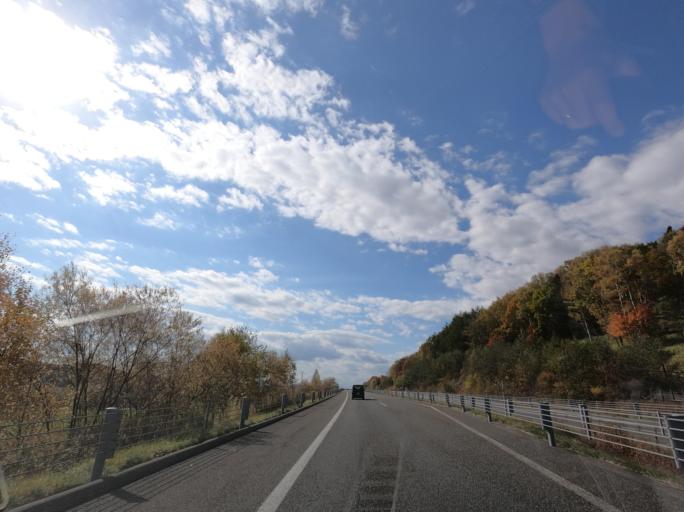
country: JP
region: Hokkaido
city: Otofuke
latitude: 43.1193
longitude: 143.6486
